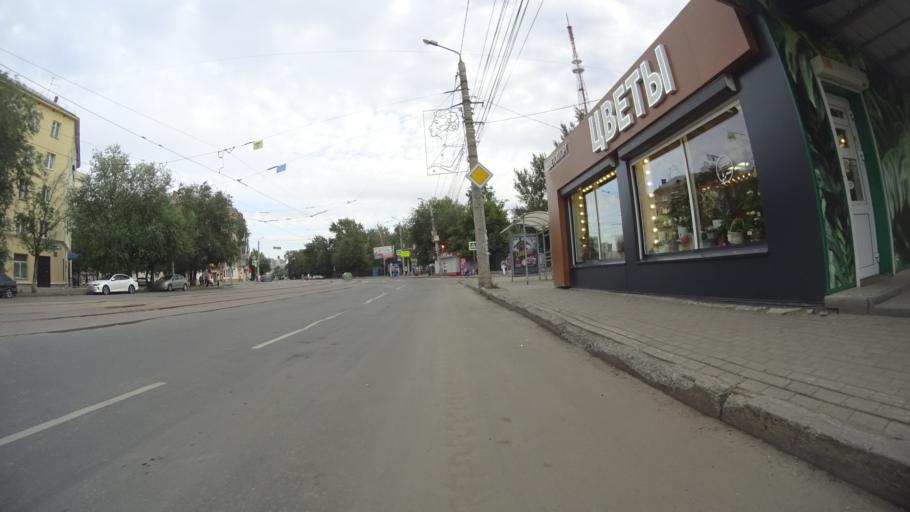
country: RU
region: Chelyabinsk
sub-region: Gorod Chelyabinsk
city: Chelyabinsk
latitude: 55.1555
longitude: 61.4068
